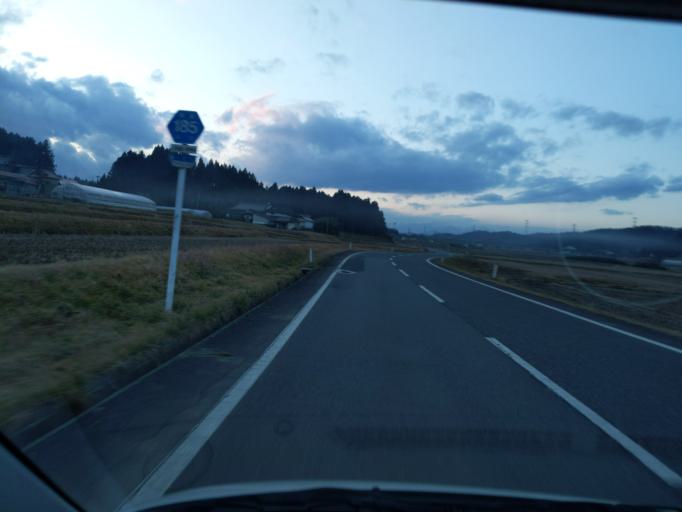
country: JP
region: Iwate
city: Ichinoseki
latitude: 38.8429
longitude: 141.1200
